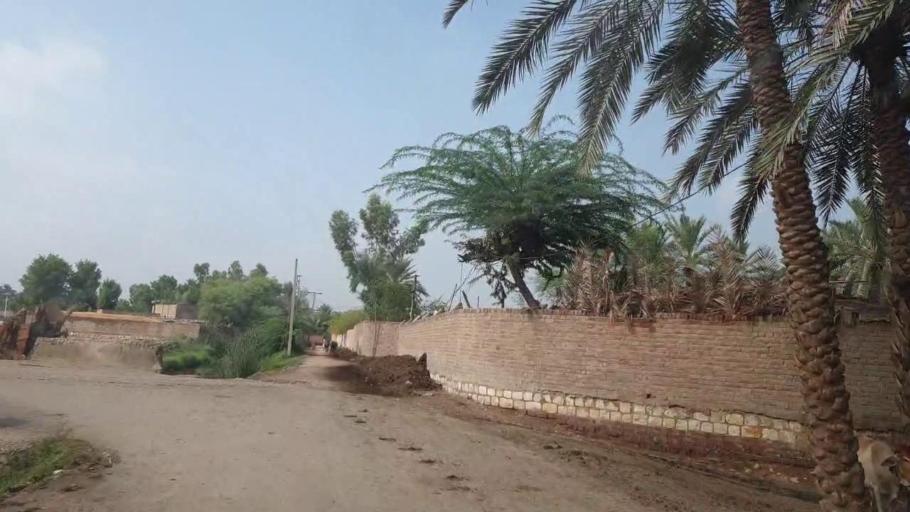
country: PK
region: Sindh
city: Khairpur
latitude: 27.5851
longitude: 68.7742
